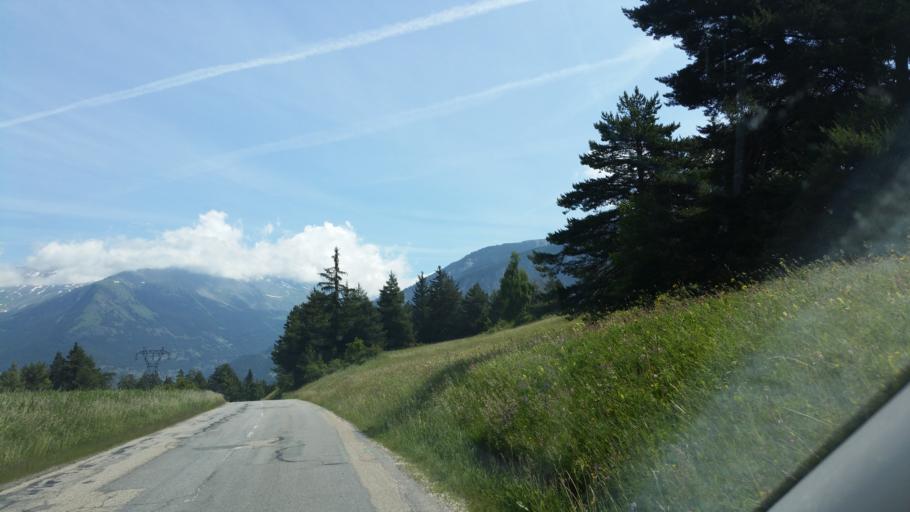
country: FR
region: Rhone-Alpes
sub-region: Departement de la Savoie
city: Modane
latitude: 45.2453
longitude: 6.7844
